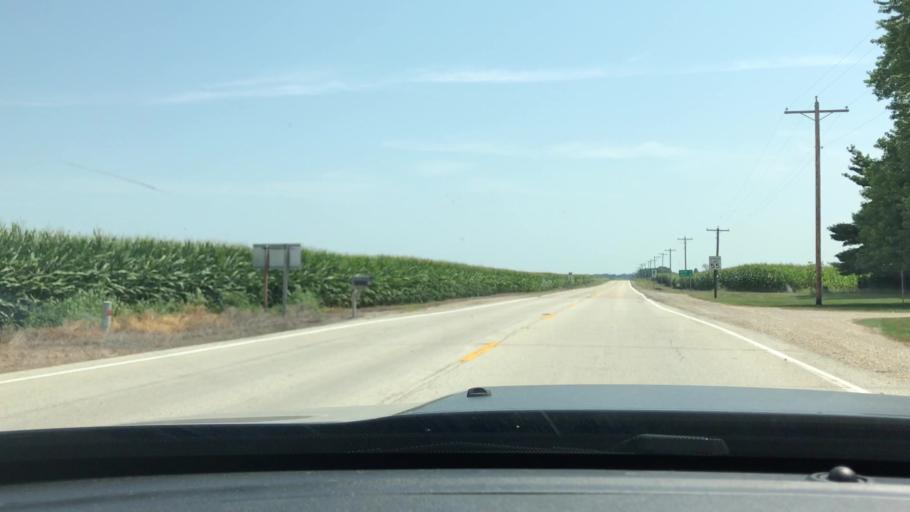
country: US
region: Illinois
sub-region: LaSalle County
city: Sheridan
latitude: 41.4854
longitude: -88.8146
